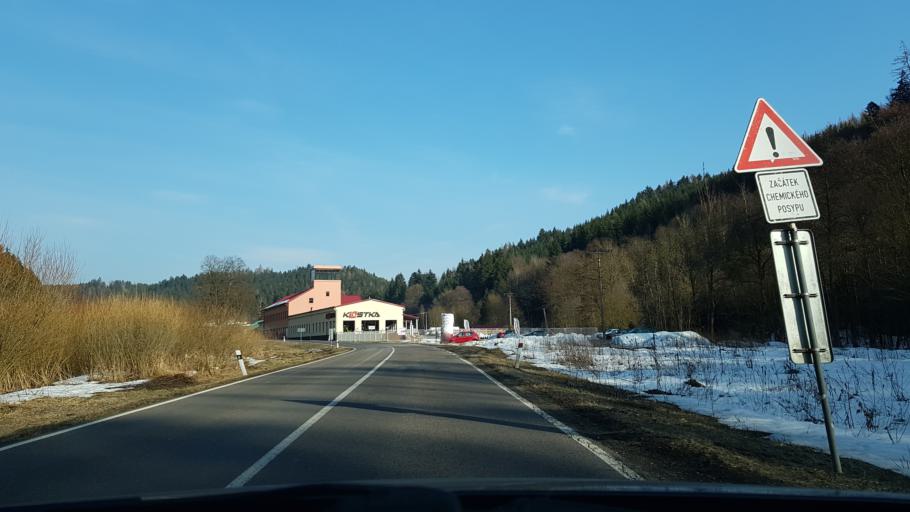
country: CZ
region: Olomoucky
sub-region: Okres Sumperk
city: Hanusovice
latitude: 50.0774
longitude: 16.9543
